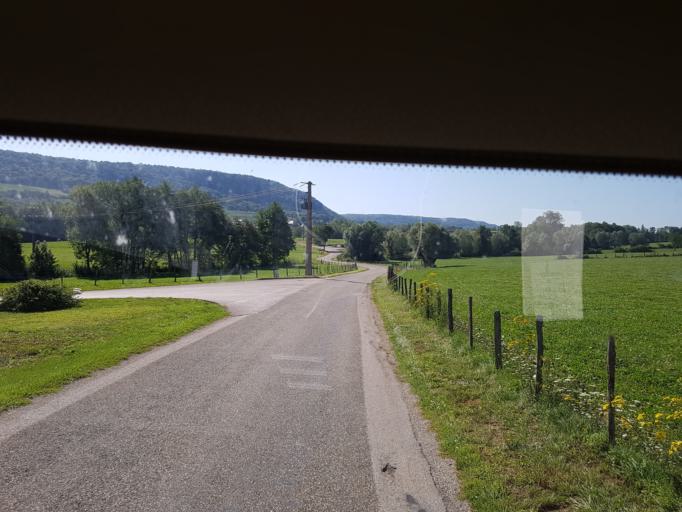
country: FR
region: Franche-Comte
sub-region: Departement du Jura
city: Perrigny
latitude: 46.7253
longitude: 5.5914
